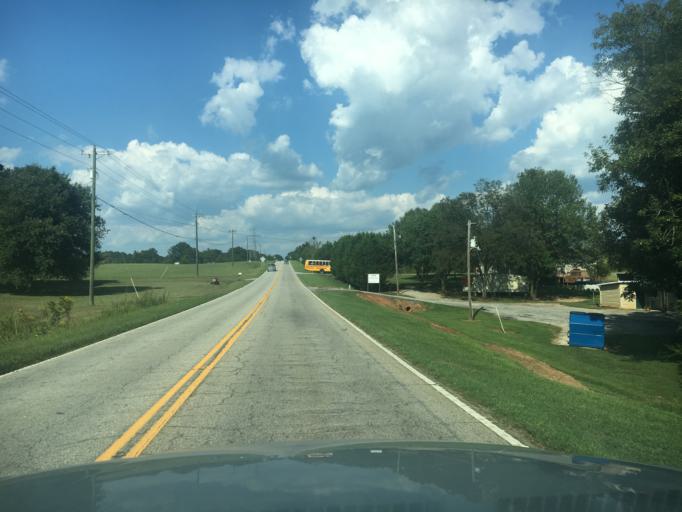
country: US
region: South Carolina
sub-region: Pickens County
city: Liberty
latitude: 34.7383
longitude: -82.6664
